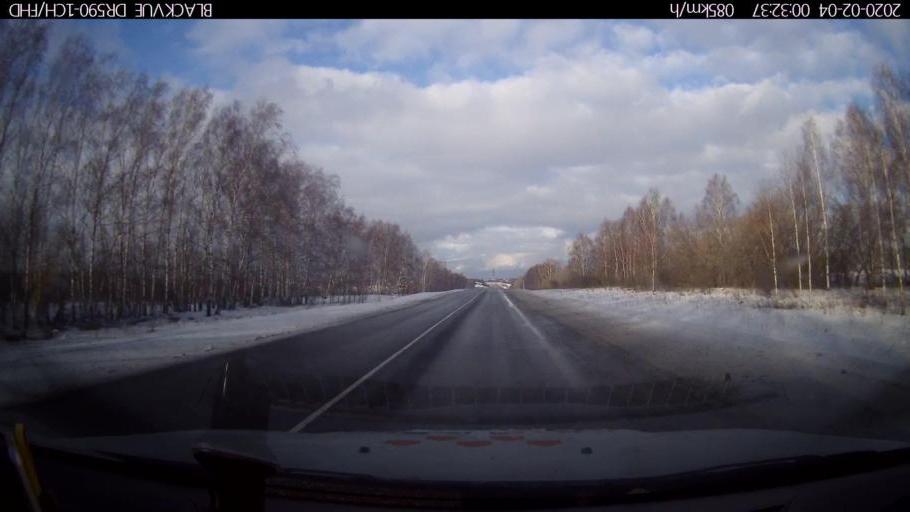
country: RU
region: Nizjnij Novgorod
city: Kstovo
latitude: 56.0611
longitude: 44.1396
